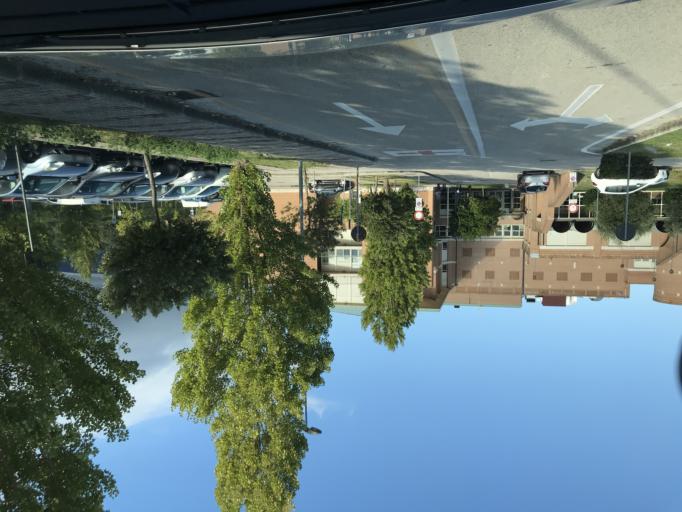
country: IT
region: Umbria
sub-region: Provincia di Perugia
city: Foligno
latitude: 42.9579
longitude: 12.6885
